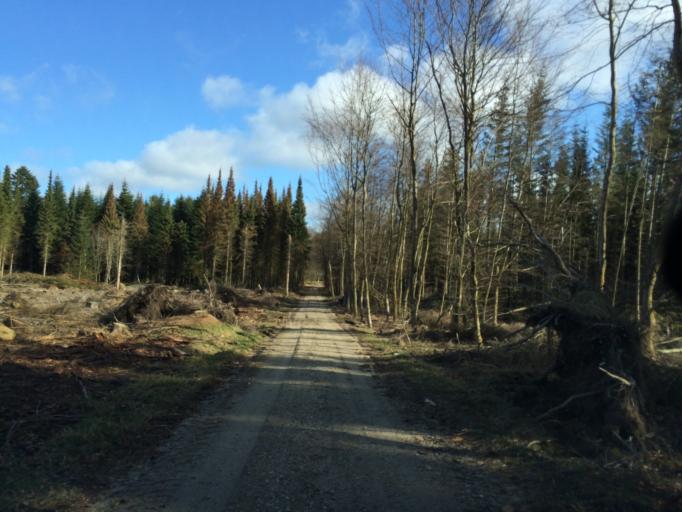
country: DK
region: Central Jutland
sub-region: Holstebro Kommune
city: Ulfborg
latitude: 56.2519
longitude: 8.4592
